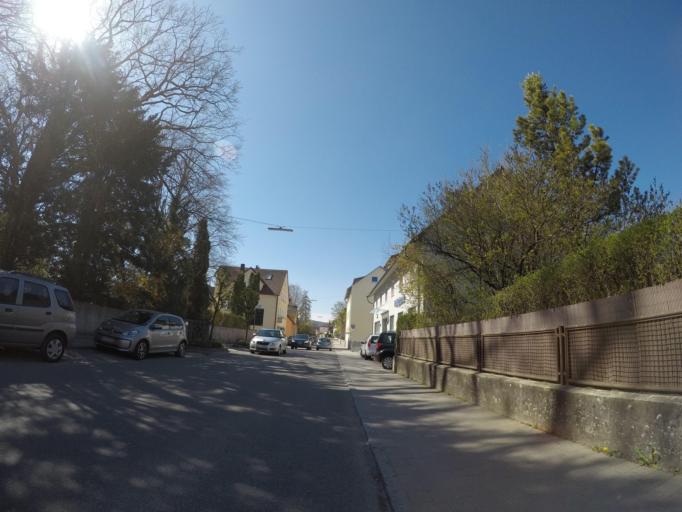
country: DE
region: Baden-Wuerttemberg
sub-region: Tuebingen Region
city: Wilhelmsdorf
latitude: 47.8658
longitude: 9.4245
